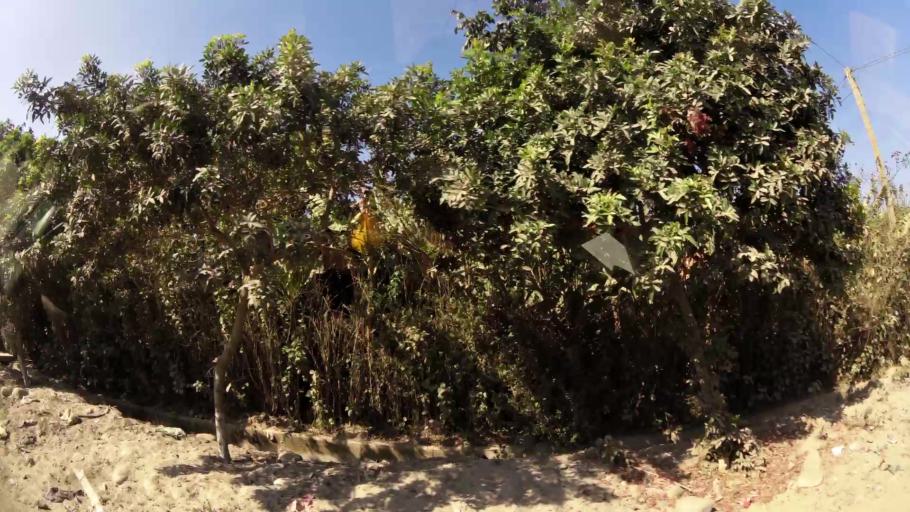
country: PE
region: Ica
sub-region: Provincia de Chincha
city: Sunampe
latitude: -13.4244
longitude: -76.1676
